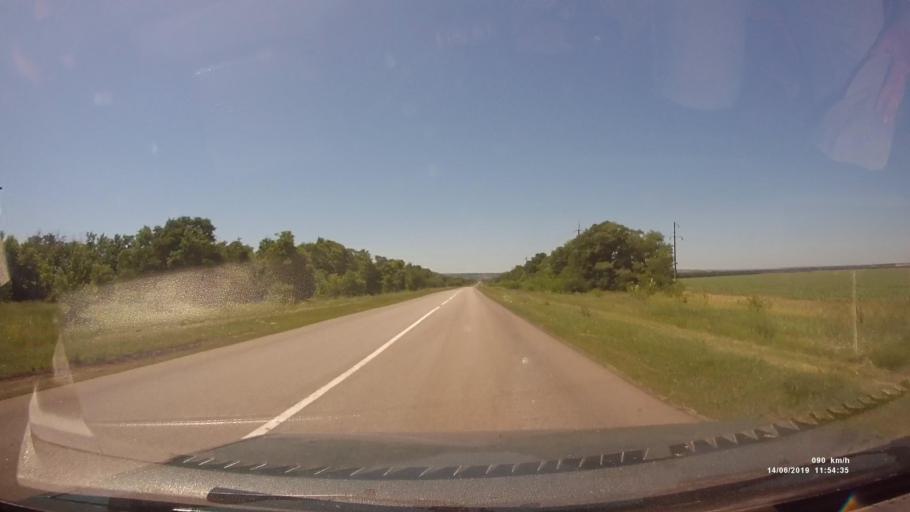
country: RU
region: Rostov
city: Kazanskaya
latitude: 49.8177
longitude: 41.1917
